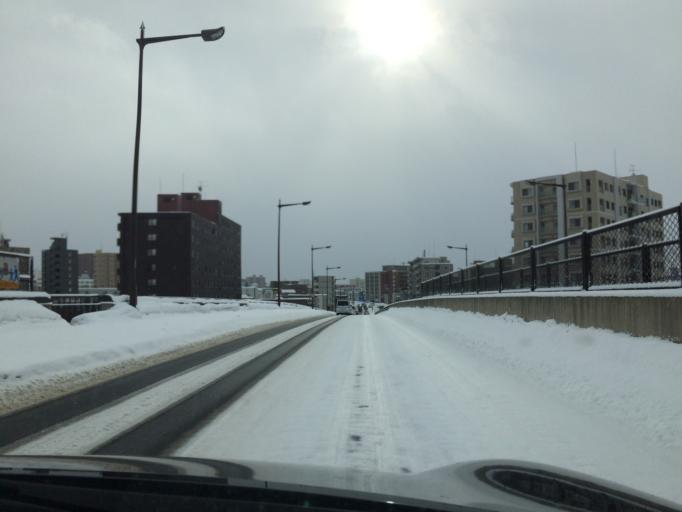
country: JP
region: Hokkaido
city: Ebetsu
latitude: 43.0475
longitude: 141.4701
